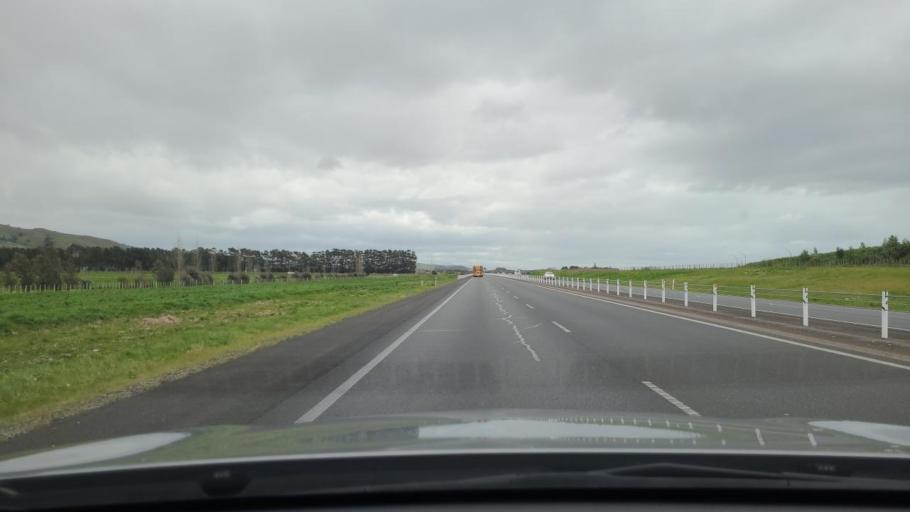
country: NZ
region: Bay of Plenty
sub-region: Western Bay of Plenty District
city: Maketu
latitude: -37.7259
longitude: 176.3249
